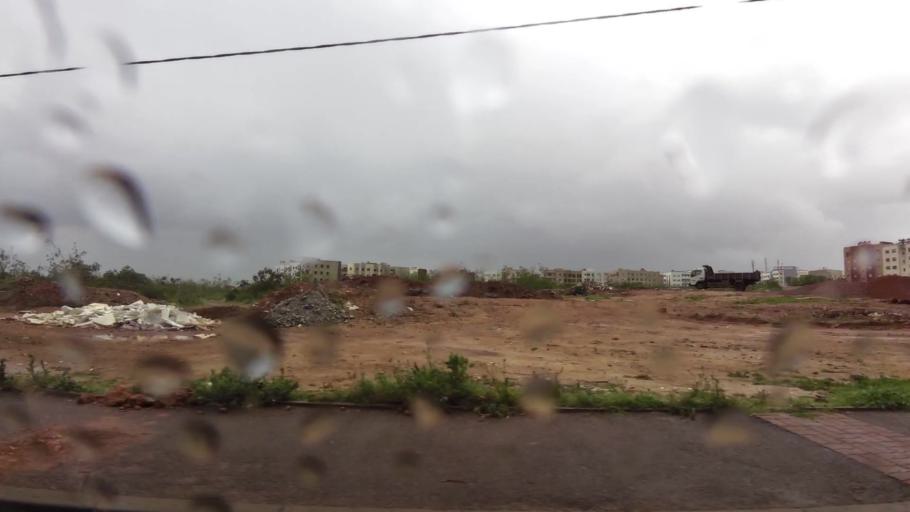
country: MA
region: Grand Casablanca
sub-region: Casablanca
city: Casablanca
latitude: 33.5411
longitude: -7.6725
